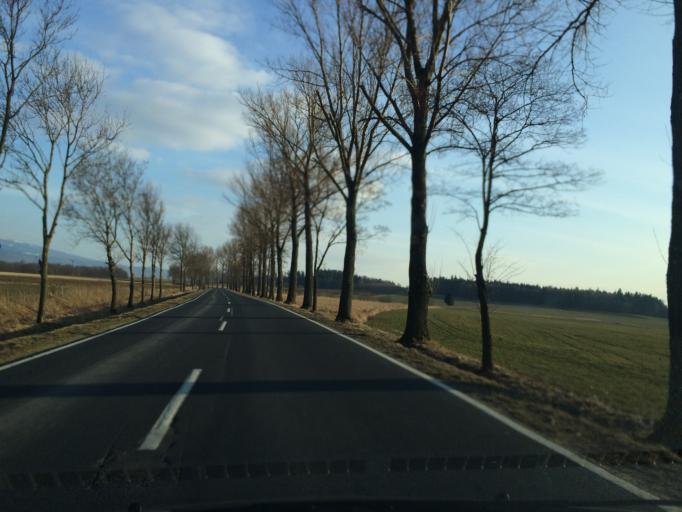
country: PL
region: Lower Silesian Voivodeship
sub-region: Powiat klodzki
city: Bystrzyca Klodzka
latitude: 50.2480
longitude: 16.6681
